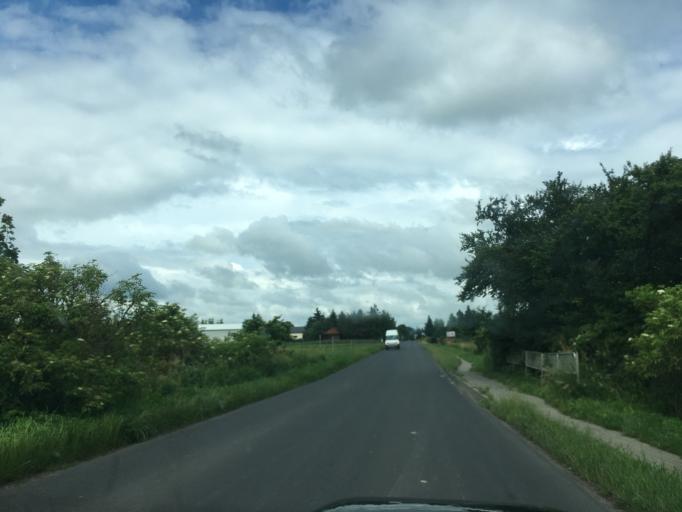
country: PL
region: Lublin Voivodeship
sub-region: Powiat swidnicki
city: Melgiew
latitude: 51.2118
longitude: 22.7464
